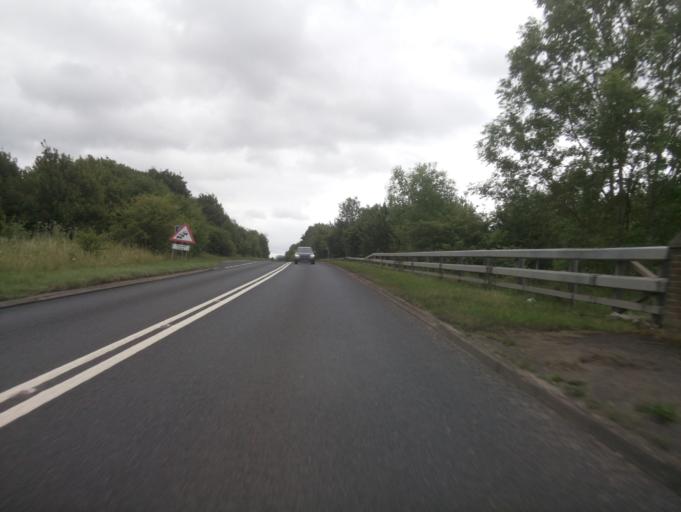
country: GB
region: England
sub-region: Worcestershire
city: Droitwich
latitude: 52.2570
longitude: -2.1720
